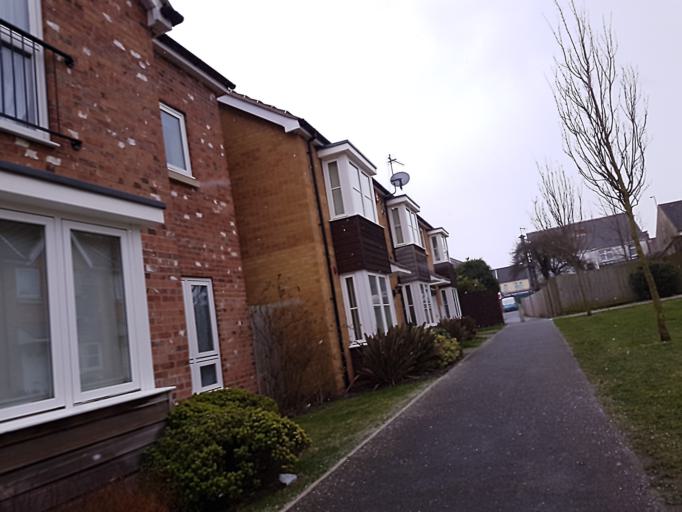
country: GB
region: England
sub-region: North East Lincolnshire
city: Grimbsy
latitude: 53.5633
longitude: -0.1117
